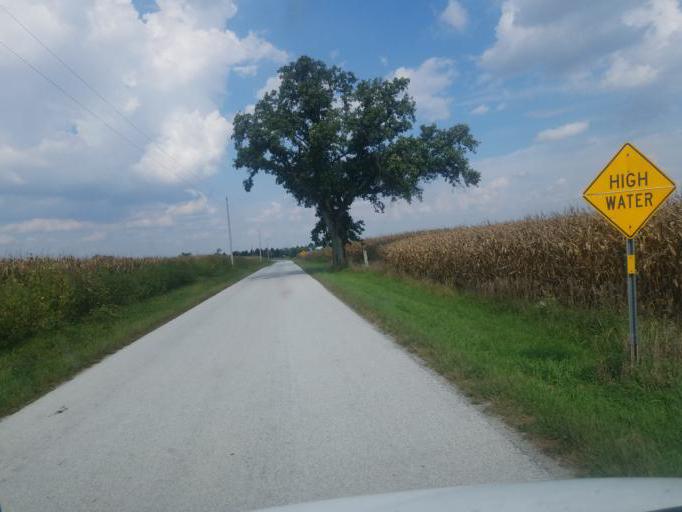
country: US
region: Ohio
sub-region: Hardin County
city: Kenton
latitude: 40.6338
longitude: -83.6532
